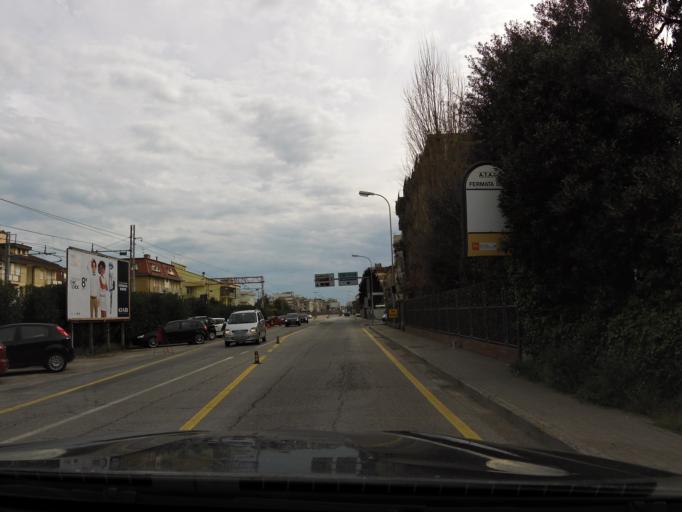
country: IT
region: The Marches
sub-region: Provincia di Macerata
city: Civitanova Marche
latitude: 43.3187
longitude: 13.7205
